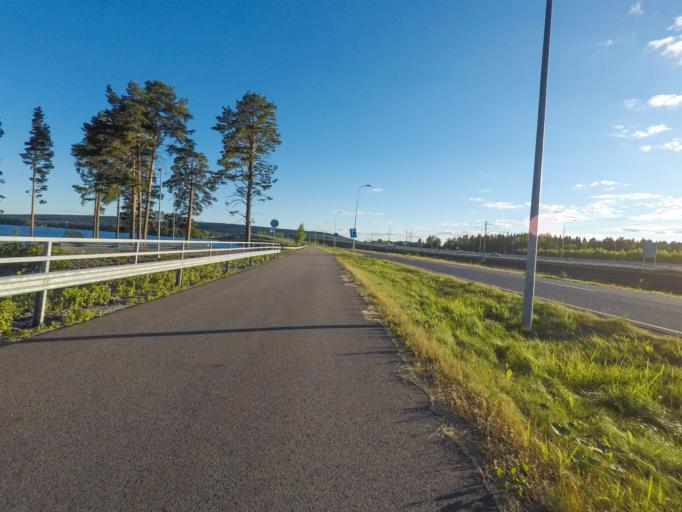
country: FI
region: Northern Savo
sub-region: Kuopio
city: Kuopio
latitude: 62.9525
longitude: 27.6820
